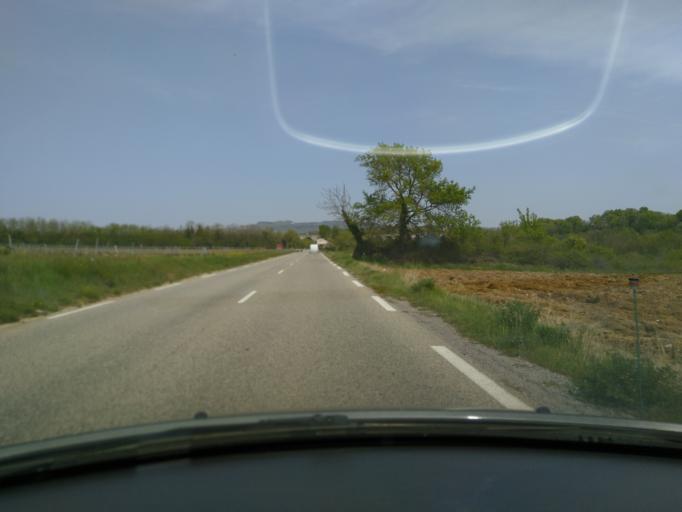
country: FR
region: Rhone-Alpes
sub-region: Departement de l'Ardeche
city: Lavilledieu
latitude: 44.5600
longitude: 4.4580
